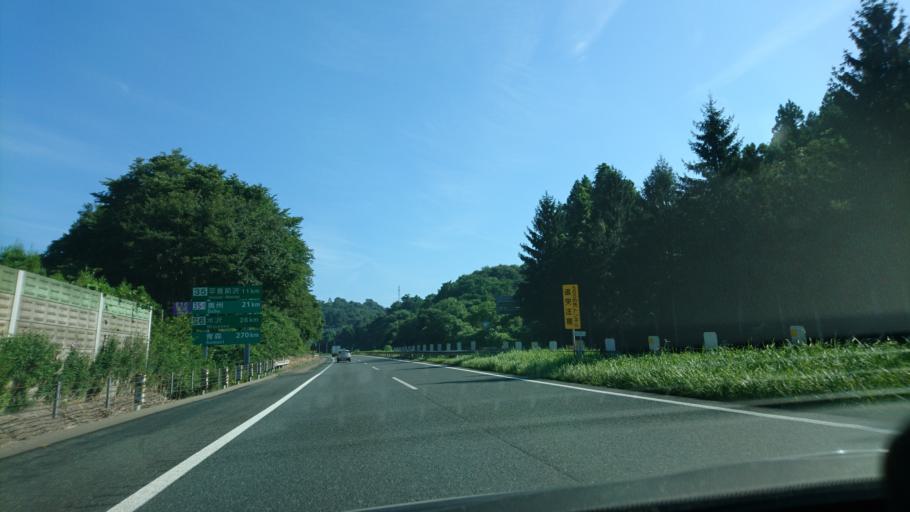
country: JP
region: Iwate
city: Ichinoseki
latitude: 38.9431
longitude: 141.1033
